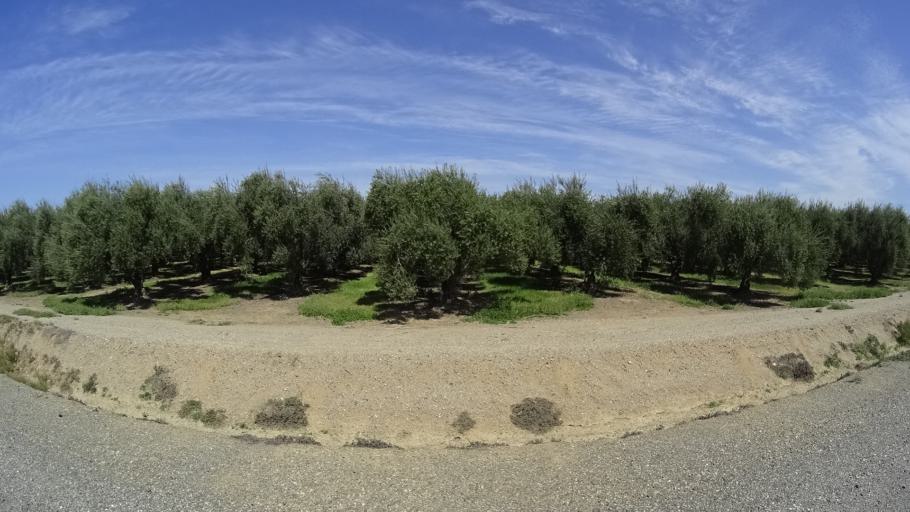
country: US
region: California
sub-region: Glenn County
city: Hamilton City
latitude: 39.6524
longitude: -122.0875
